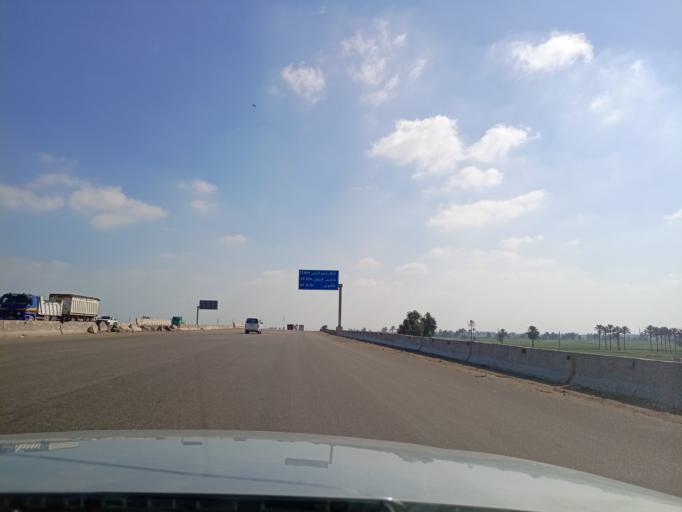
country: EG
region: Eastern Province
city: Mashtul as Suq
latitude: 30.4619
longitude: 31.3803
